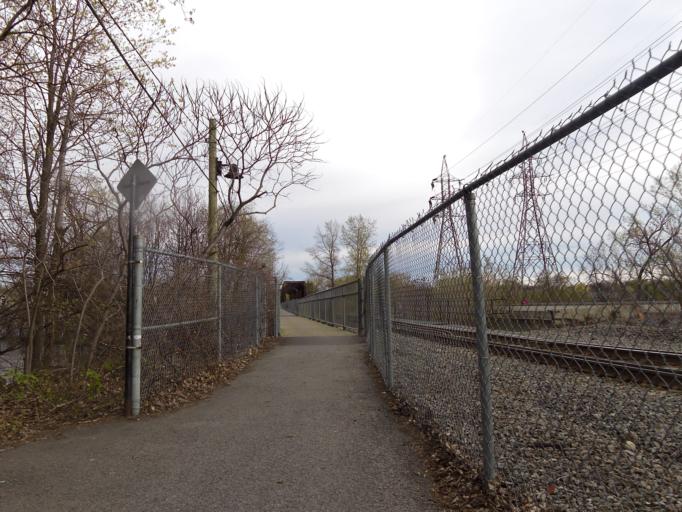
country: CA
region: Quebec
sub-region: Laval
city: Laval
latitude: 45.5467
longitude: -73.6983
